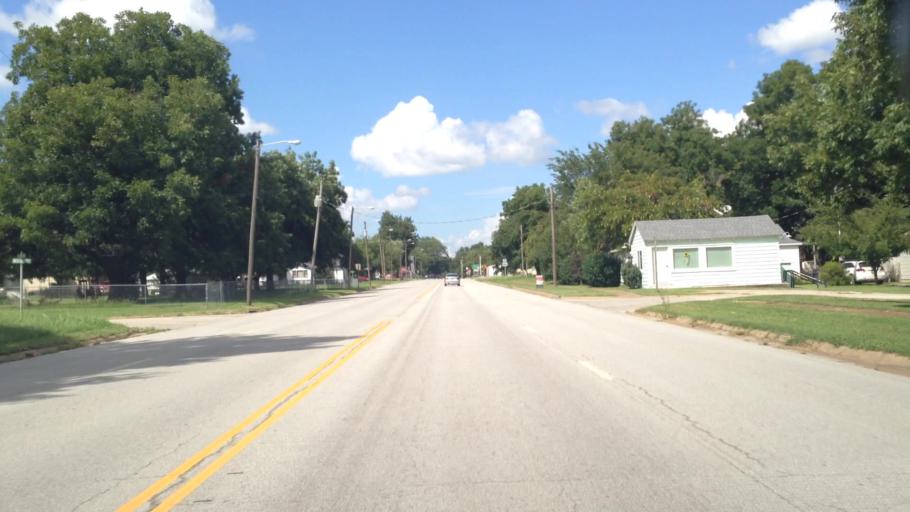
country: US
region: Kansas
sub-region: Labette County
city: Chetopa
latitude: 37.0337
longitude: -95.0863
